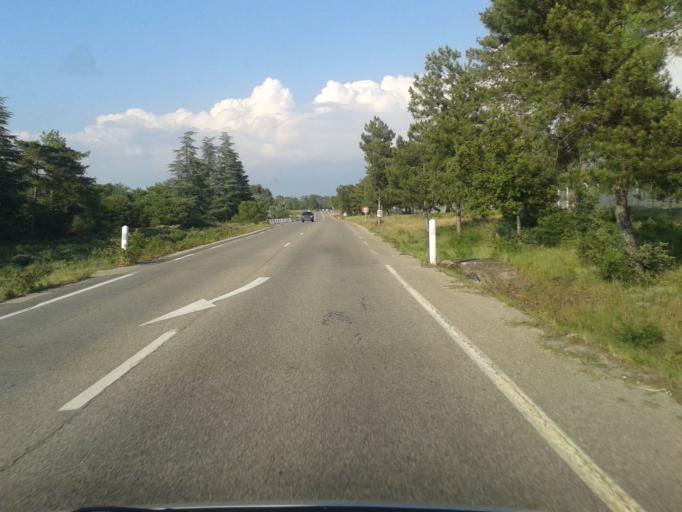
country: FR
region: Provence-Alpes-Cote d'Azur
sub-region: Departement du Var
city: Vinon-sur-Verdon
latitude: 43.7065
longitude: 5.7573
